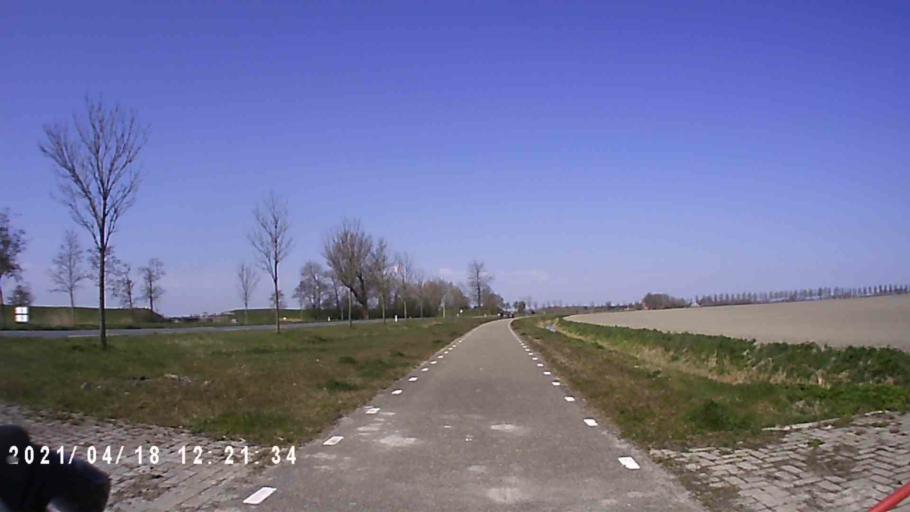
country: NL
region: Friesland
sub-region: Gemeente Kollumerland en Nieuwkruisland
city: Kollum
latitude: 53.3218
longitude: 6.1327
